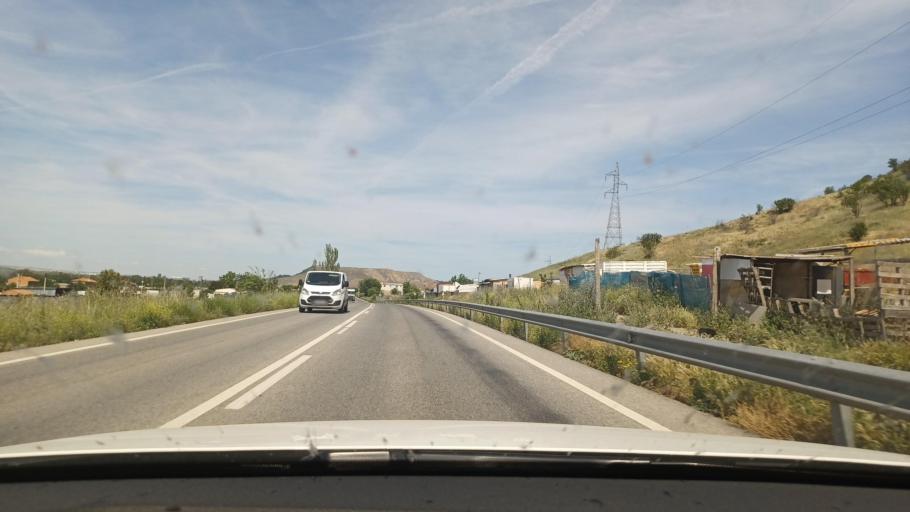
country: ES
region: Madrid
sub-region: Provincia de Madrid
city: Torrejon de Ardoz
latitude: 40.4240
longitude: -3.4559
